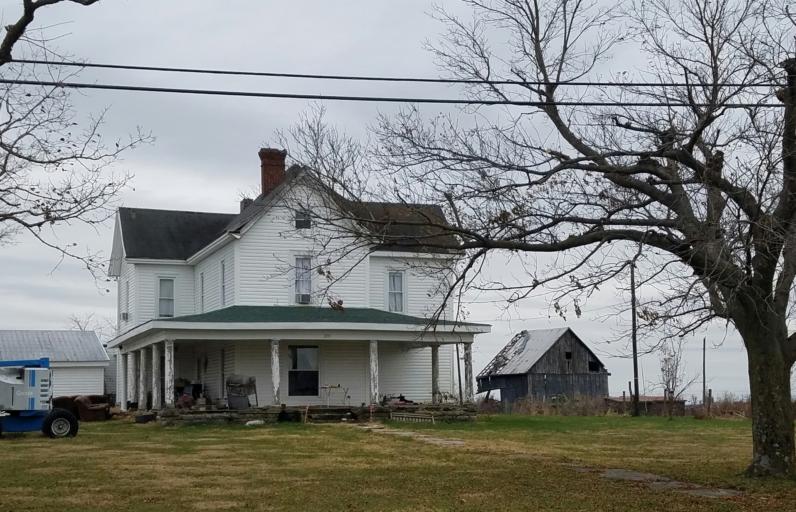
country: US
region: Kentucky
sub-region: Henry County
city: Eminence
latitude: 38.3496
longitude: -85.1237
